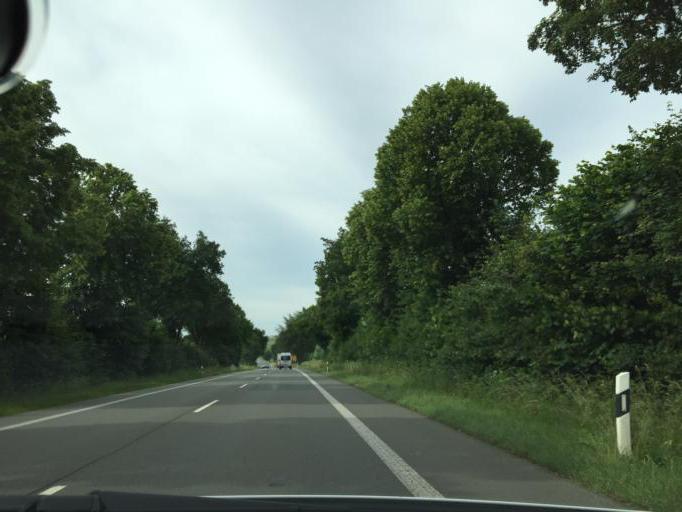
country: DE
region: North Rhine-Westphalia
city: Warburg
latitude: 51.5573
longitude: 9.1333
